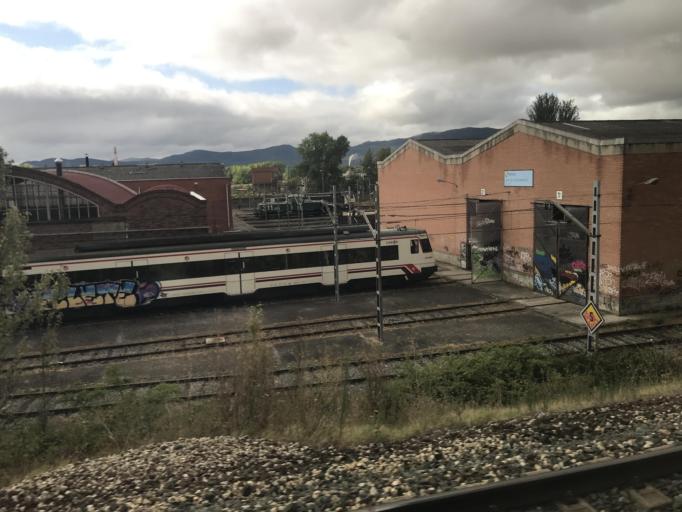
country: ES
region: Castille and Leon
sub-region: Provincia de Burgos
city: Miranda de Ebro
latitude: 42.6947
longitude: -2.9309
